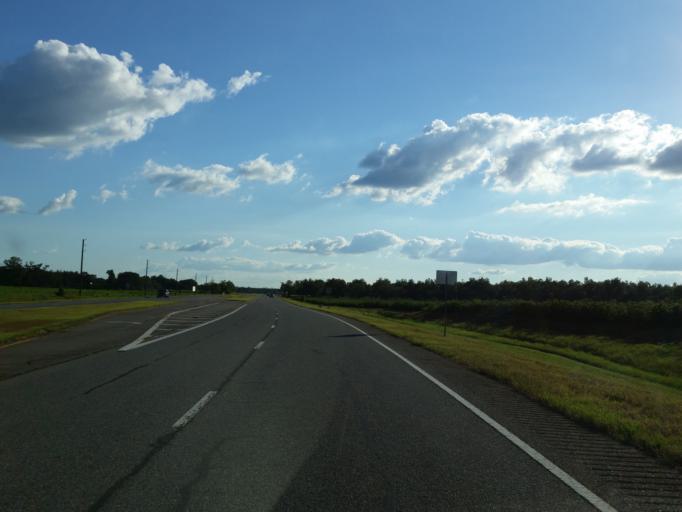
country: US
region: Georgia
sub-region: Houston County
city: Perry
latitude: 32.4884
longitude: -83.7649
